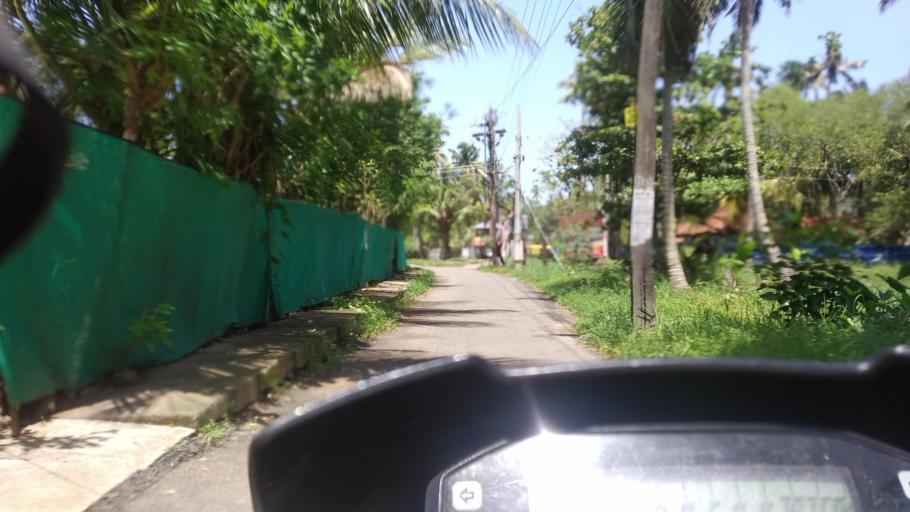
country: IN
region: Kerala
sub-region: Ernakulam
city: Elur
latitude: 10.0726
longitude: 76.2080
